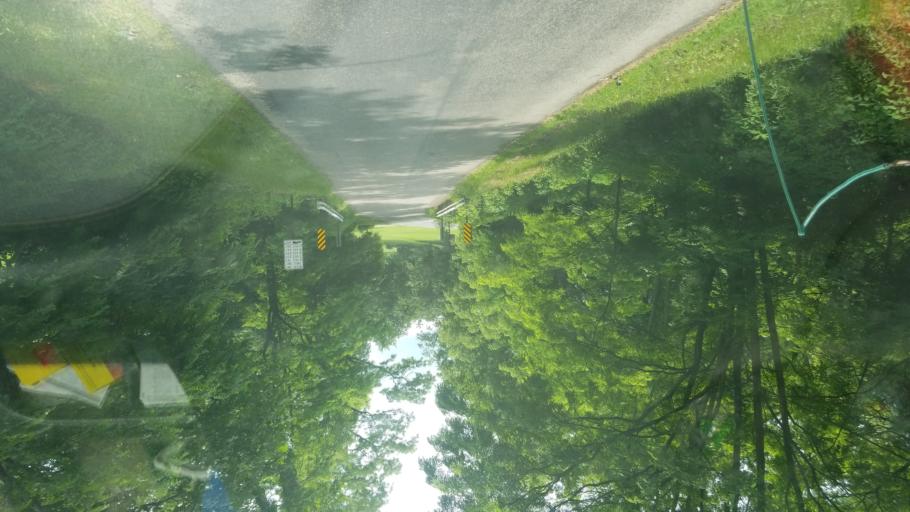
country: US
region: Ohio
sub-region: Wayne County
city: West Salem
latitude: 40.8362
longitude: -82.1066
